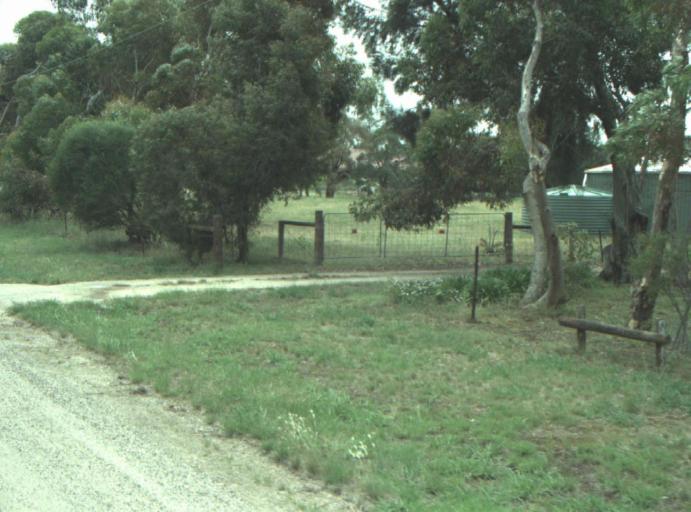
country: AU
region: Victoria
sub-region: Greater Geelong
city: Lara
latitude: -38.0018
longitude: 144.4190
